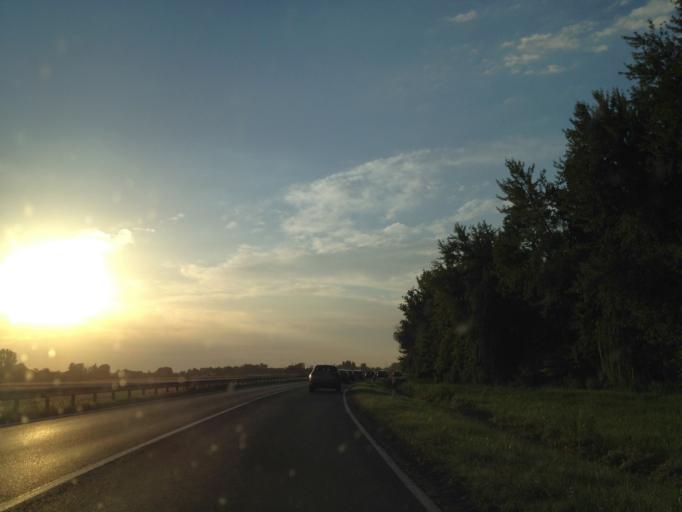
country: HU
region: Gyor-Moson-Sopron
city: Mosonmagyarovar
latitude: 47.8309
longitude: 17.2995
